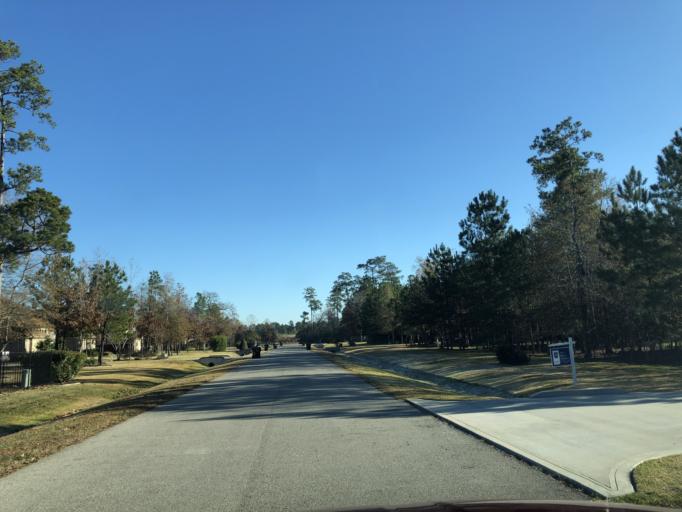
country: US
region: Texas
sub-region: Montgomery County
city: Porter Heights
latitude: 30.0682
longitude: -95.3210
